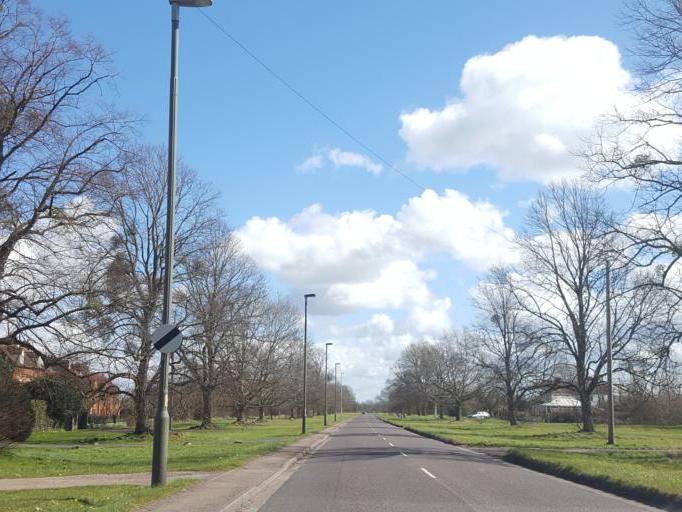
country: GB
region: England
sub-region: Worcestershire
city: Great Malvern
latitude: 52.1065
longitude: -2.2937
